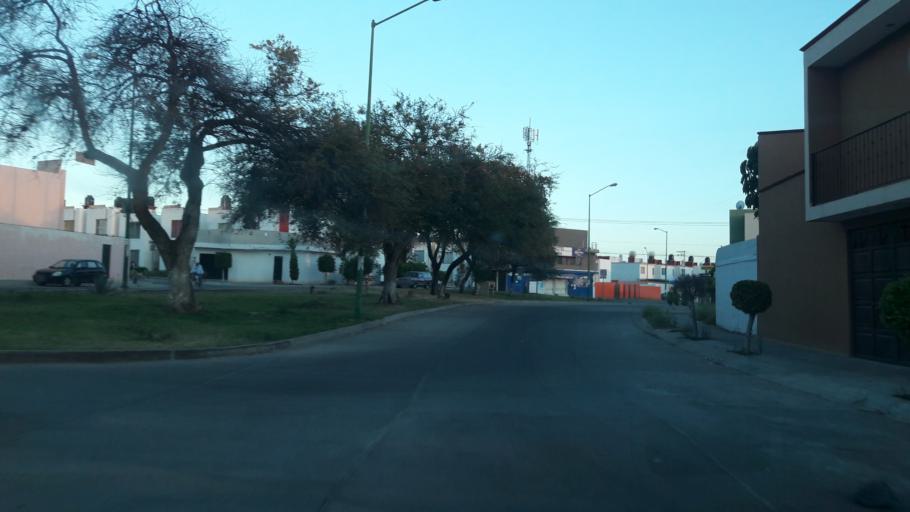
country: MX
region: Guanajuato
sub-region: Leon
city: Medina
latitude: 21.1672
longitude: -101.6320
